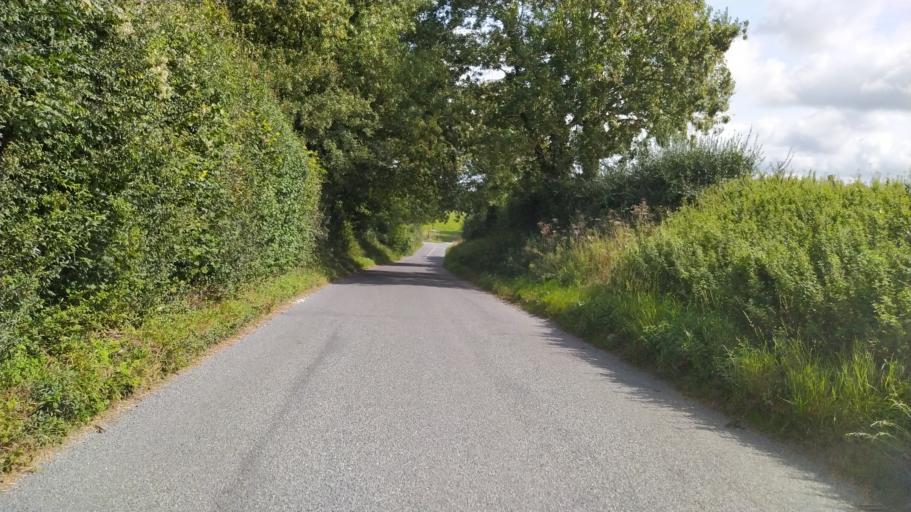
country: GB
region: England
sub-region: Dorset
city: Blandford Forum
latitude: 50.8248
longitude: -2.1123
